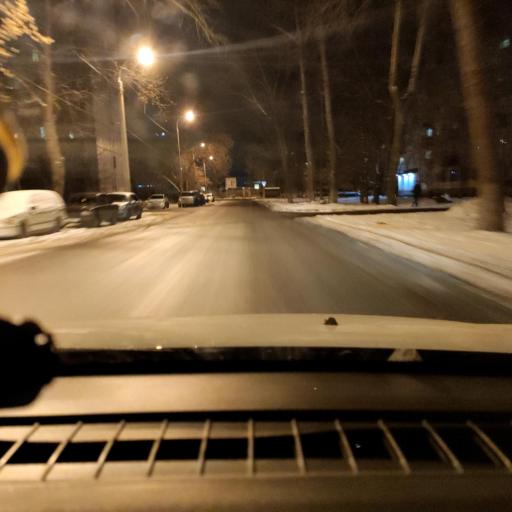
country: RU
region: Samara
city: Samara
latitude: 53.1161
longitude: 50.0701
